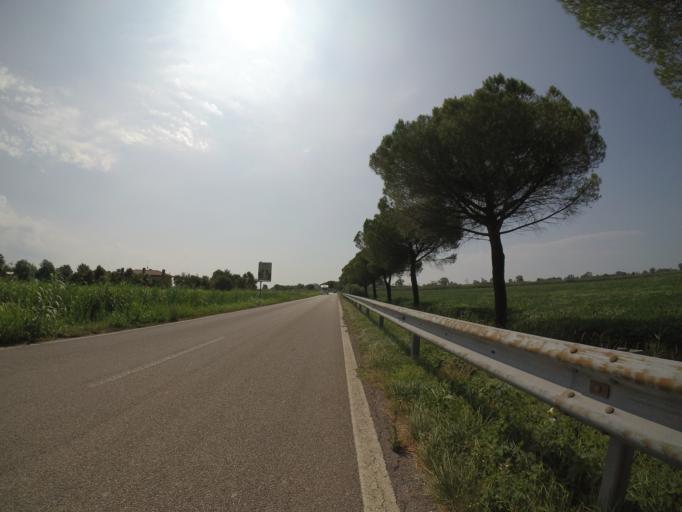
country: IT
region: Friuli Venezia Giulia
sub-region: Provincia di Udine
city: Pertegada
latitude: 45.6840
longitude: 13.0590
